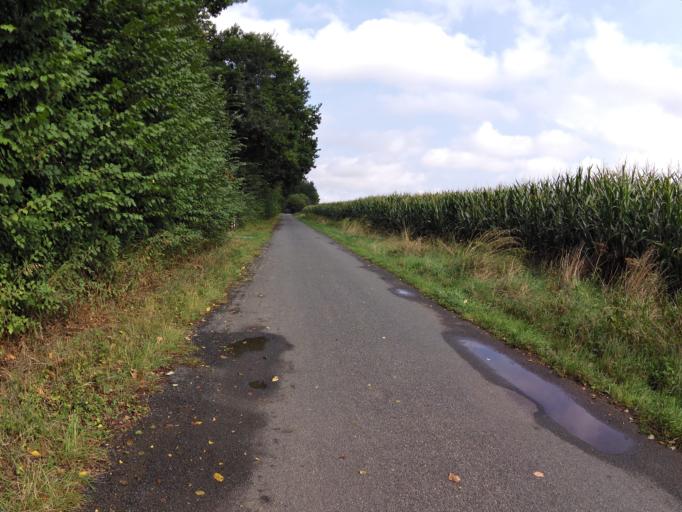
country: DE
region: Lower Saxony
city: Balge
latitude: 52.7194
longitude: 9.1938
